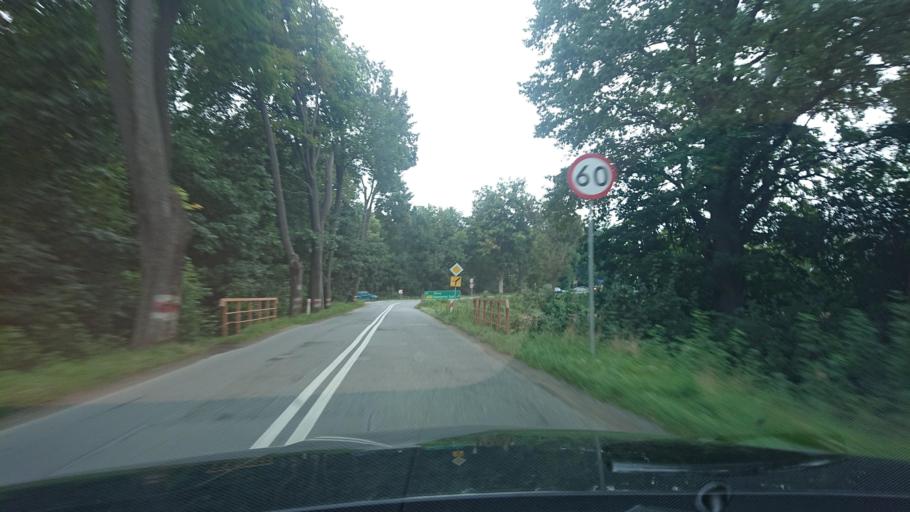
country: PL
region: Lower Silesian Voivodeship
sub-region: Powiat zabkowicki
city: Kamieniec Zabkowicki
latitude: 50.5112
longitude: 16.8694
